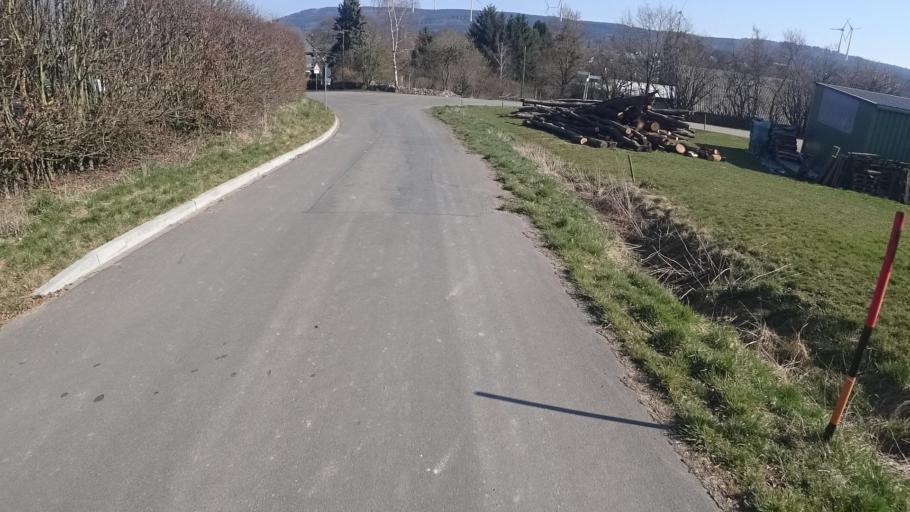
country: DE
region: Rheinland-Pfalz
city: Schnorbach
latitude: 49.9856
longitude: 7.6364
